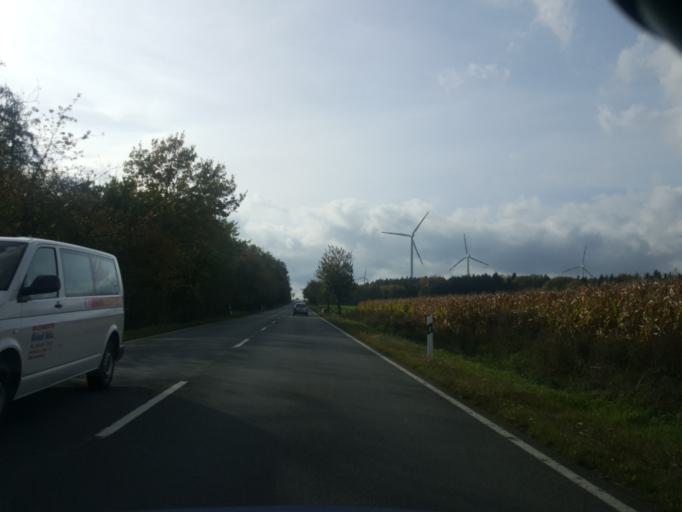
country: DE
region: Saxony-Anhalt
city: Hergisdorf
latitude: 51.5114
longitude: 11.4815
